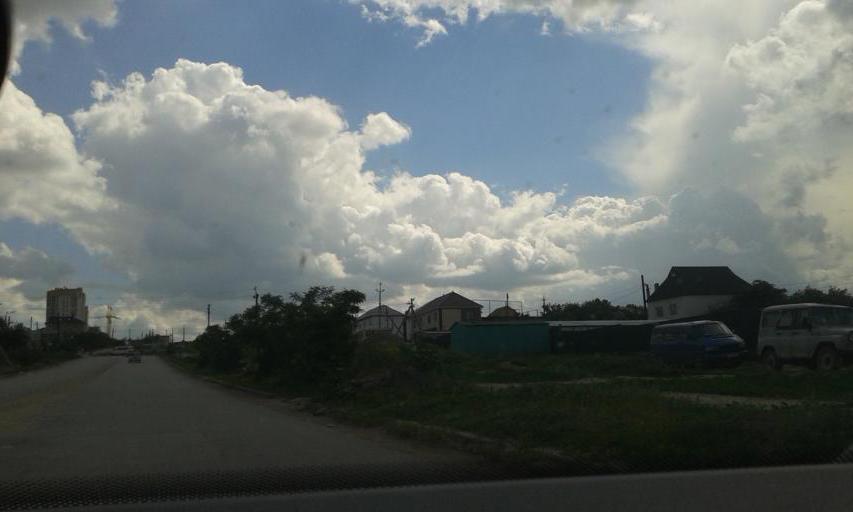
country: RU
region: Volgograd
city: Volgograd
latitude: 48.6523
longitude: 44.4124
